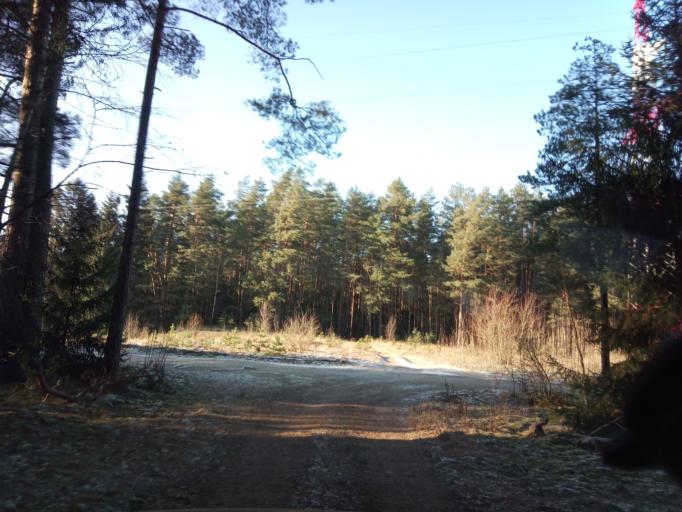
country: LT
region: Alytaus apskritis
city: Druskininkai
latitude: 53.9546
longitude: 23.8617
